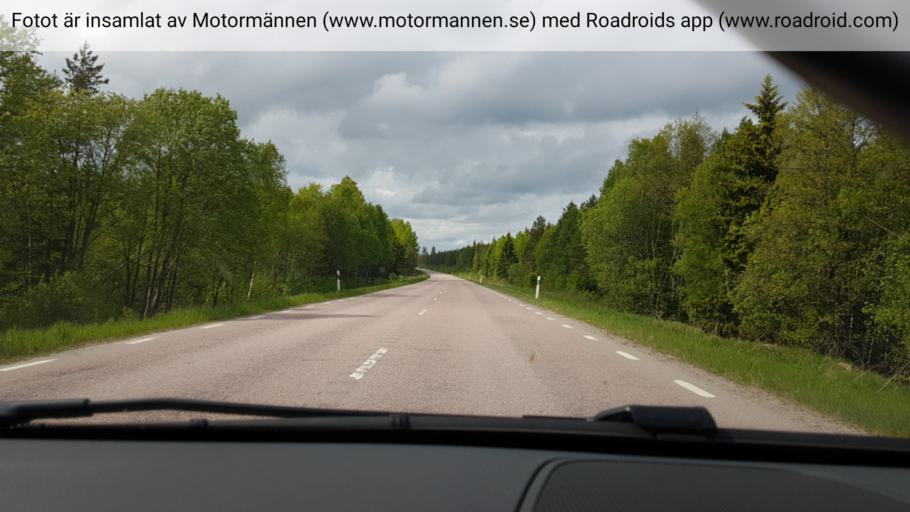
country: SE
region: Uppsala
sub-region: Tierps Kommun
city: Tierp
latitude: 60.2873
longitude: 17.5860
